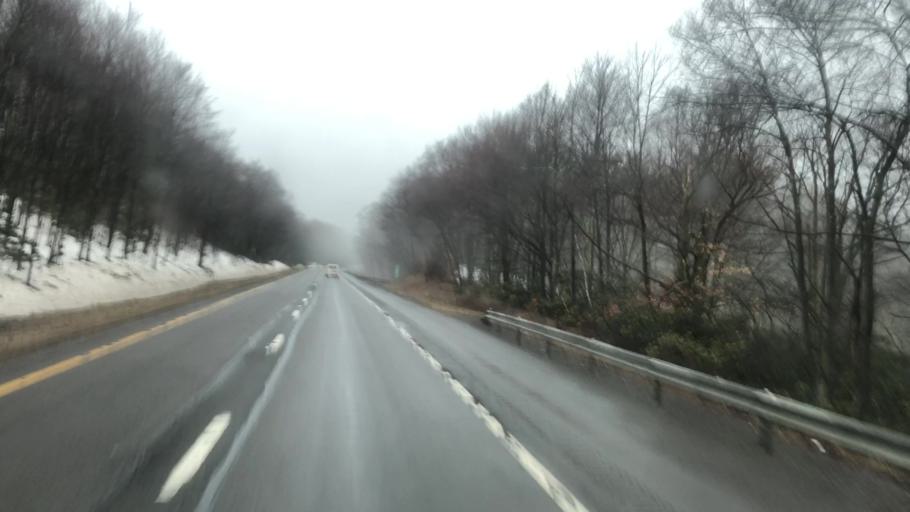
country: US
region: Pennsylvania
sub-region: Carbon County
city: Towamensing Trails
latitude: 41.0805
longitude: -75.6040
